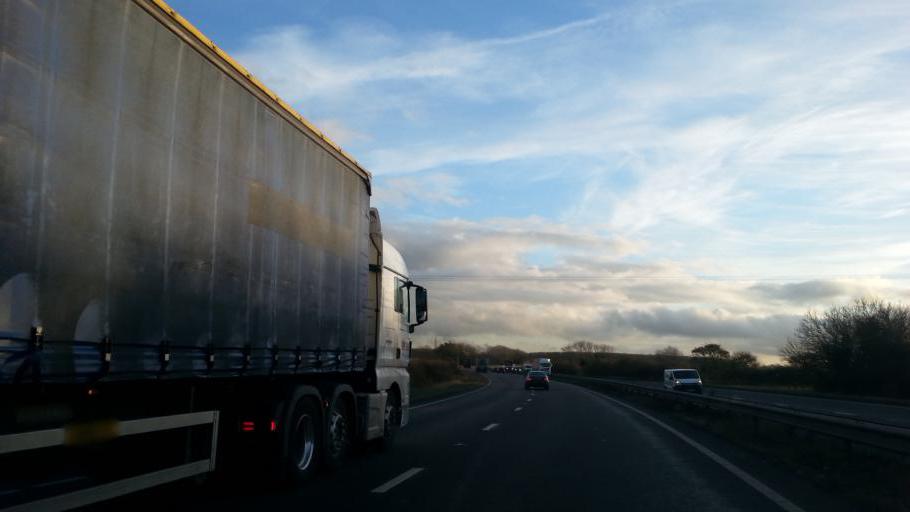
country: GB
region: England
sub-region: Northamptonshire
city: Brackley
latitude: 52.0078
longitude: -1.1595
